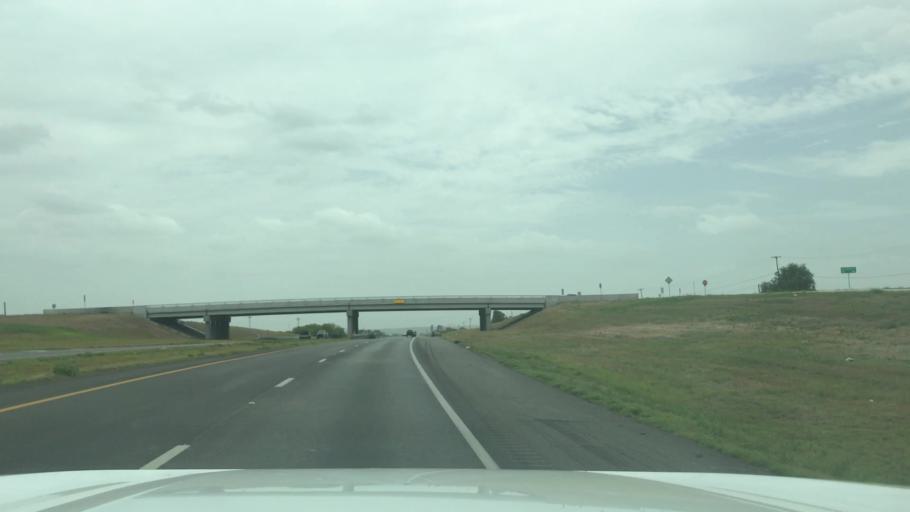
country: US
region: Texas
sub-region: McLennan County
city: Woodway
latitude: 31.5740
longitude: -97.2891
